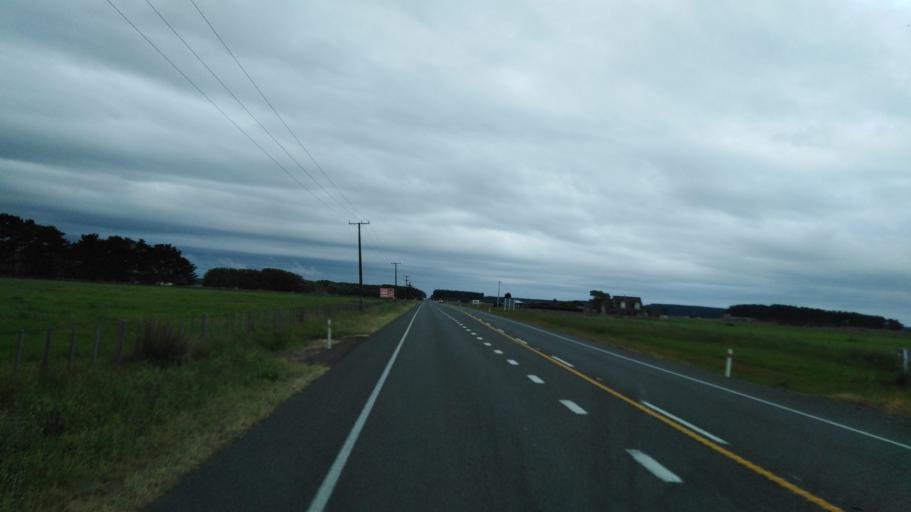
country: NZ
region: Manawatu-Wanganui
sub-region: Horowhenua District
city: Foxton
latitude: -40.3951
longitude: 175.3139
